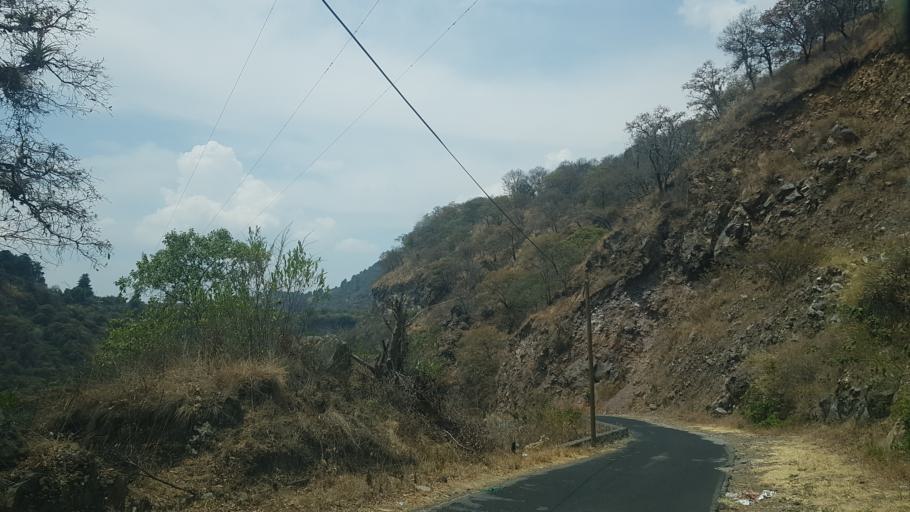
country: MX
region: Puebla
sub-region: Tochimilco
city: La Magdalena Yancuitlalpan
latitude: 18.8741
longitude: -98.6030
